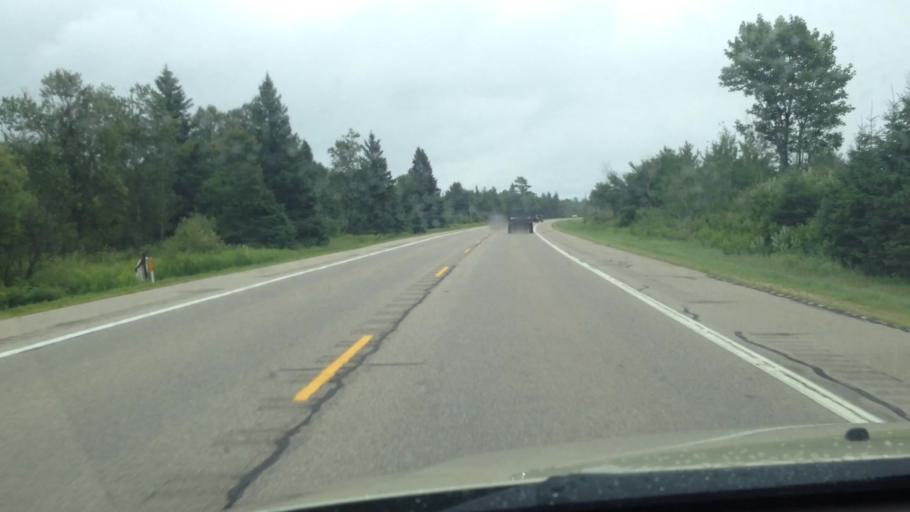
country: US
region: Michigan
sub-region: Schoolcraft County
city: Manistique
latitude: 45.9003
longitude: -86.5624
